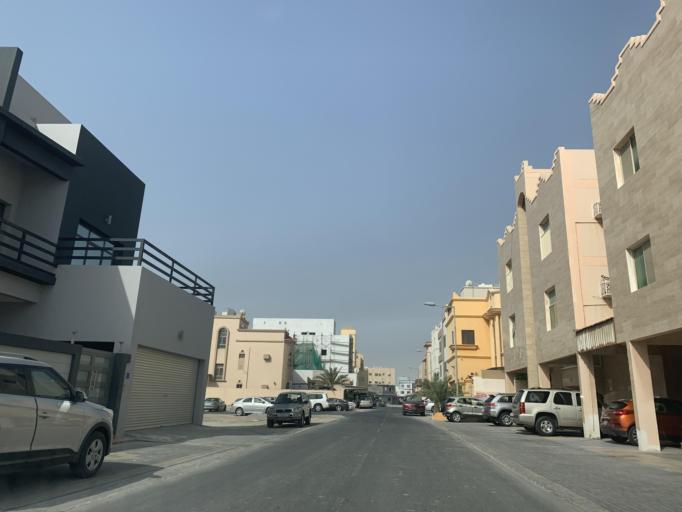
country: BH
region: Northern
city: Madinat `Isa
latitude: 26.1883
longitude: 50.5624
